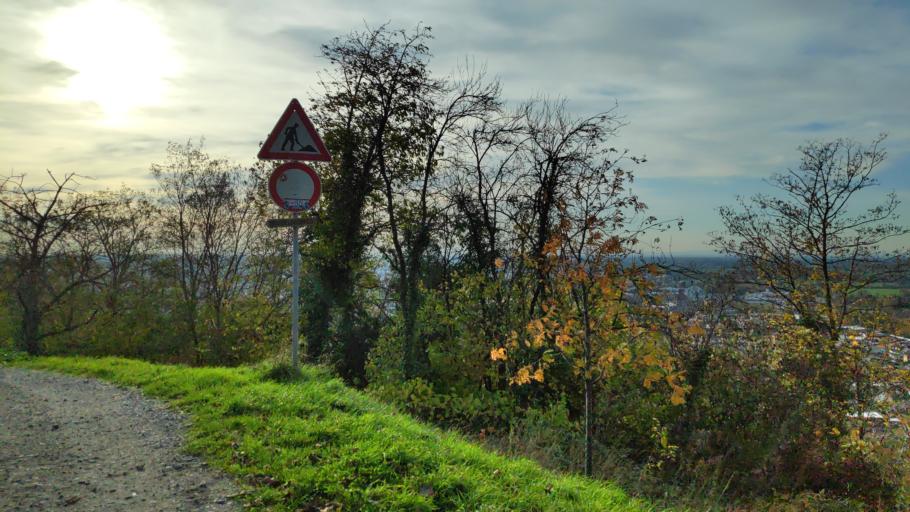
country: DE
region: Hesse
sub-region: Regierungsbezirk Darmstadt
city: Heppenheim an der Bergstrasse
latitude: 49.6480
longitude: 8.6422
